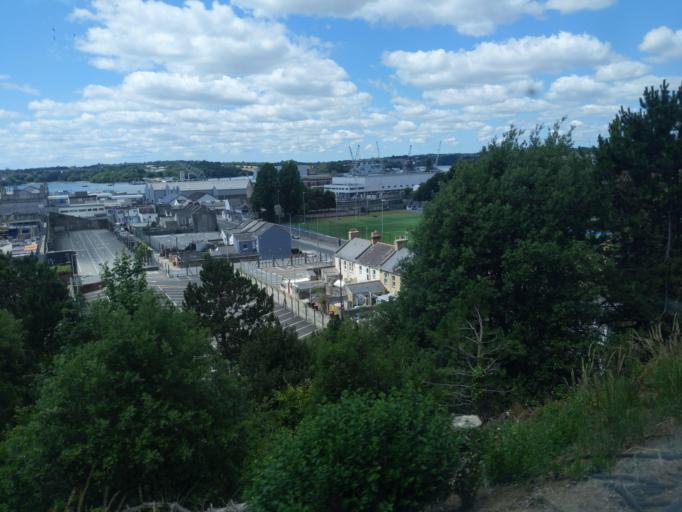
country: GB
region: England
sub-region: Cornwall
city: Millbrook
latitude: 50.3836
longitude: -4.1765
